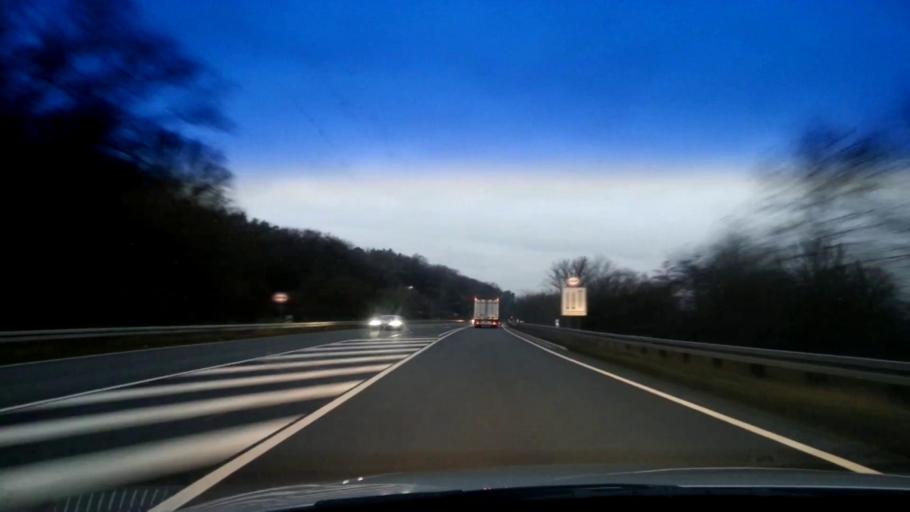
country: DE
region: Bavaria
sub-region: Upper Franconia
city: Strullendorf
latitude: 49.8199
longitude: 10.9601
